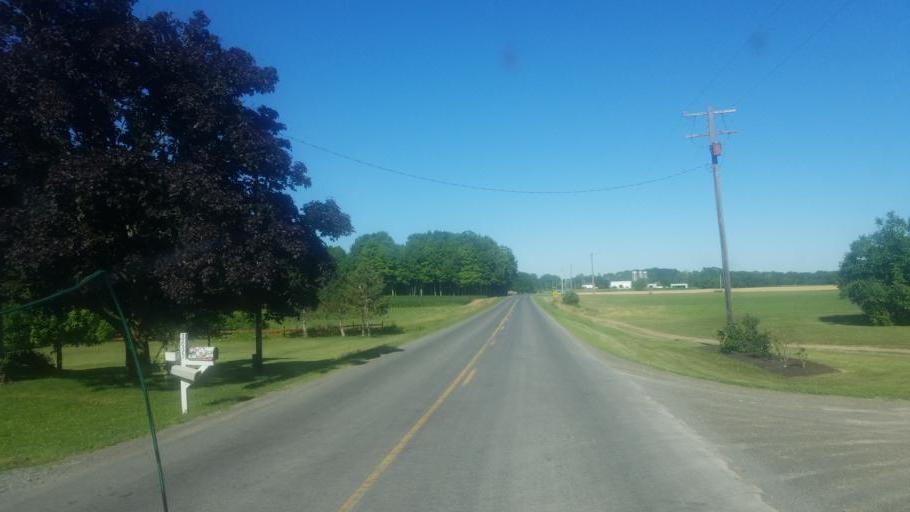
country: US
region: New York
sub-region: Ontario County
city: Canandaigua
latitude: 42.8359
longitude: -77.1965
